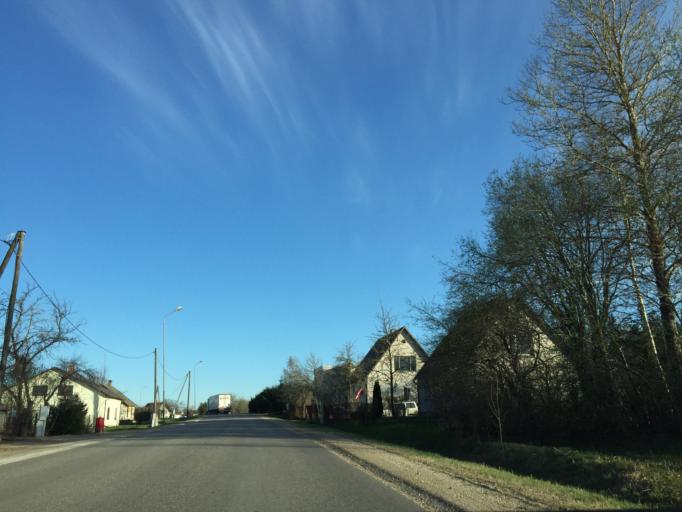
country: LV
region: Valkas Rajons
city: Valka
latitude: 57.7688
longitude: 26.0006
